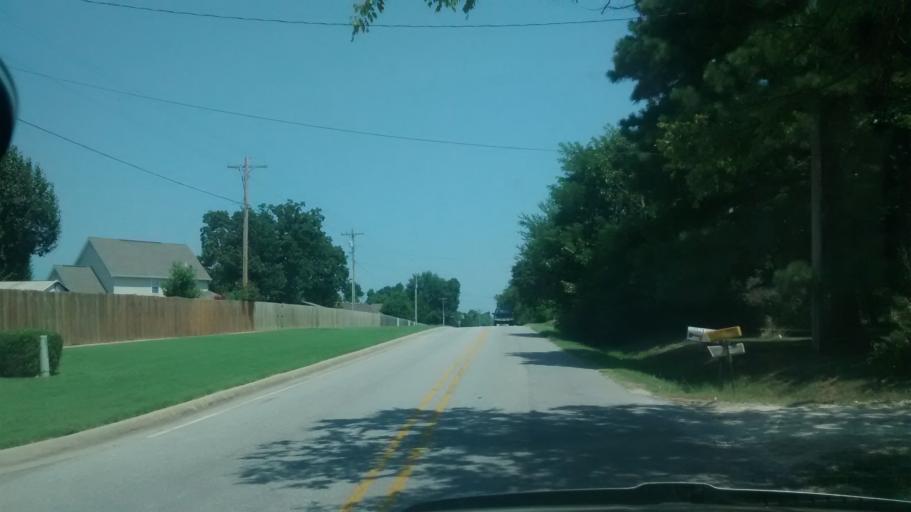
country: US
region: Arkansas
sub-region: Washington County
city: Farmington
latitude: 36.0683
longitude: -94.2534
